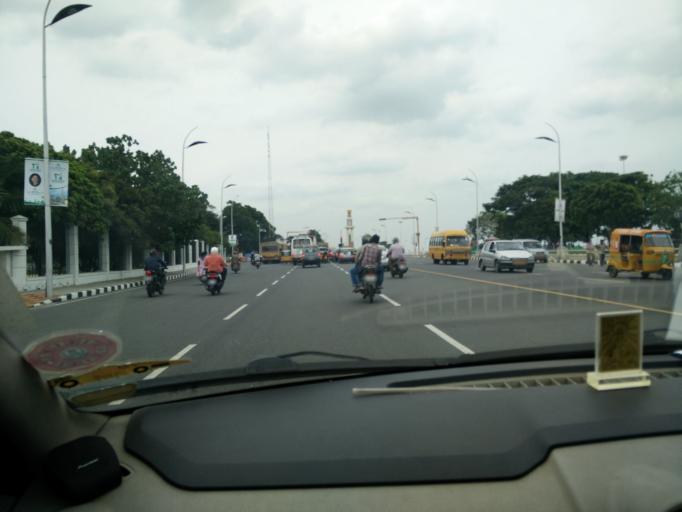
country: IN
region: Tamil Nadu
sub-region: Chennai
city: Gandhi Nagar
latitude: 13.0421
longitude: 80.2794
